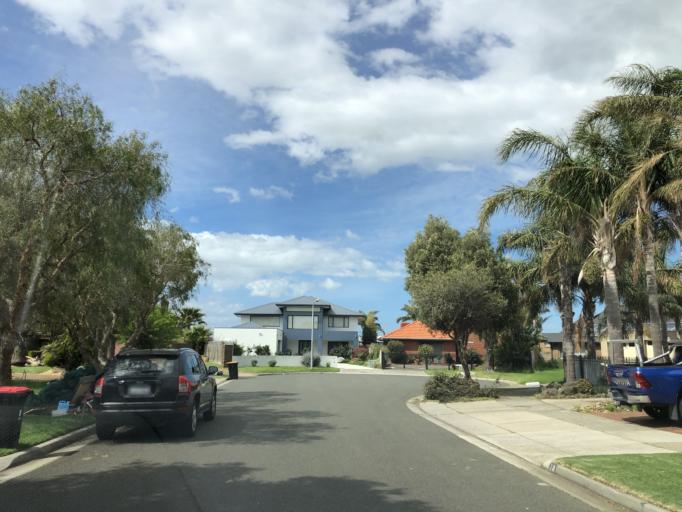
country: AU
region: Victoria
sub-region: Kingston
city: Carrum
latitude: -38.0756
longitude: 145.1367
